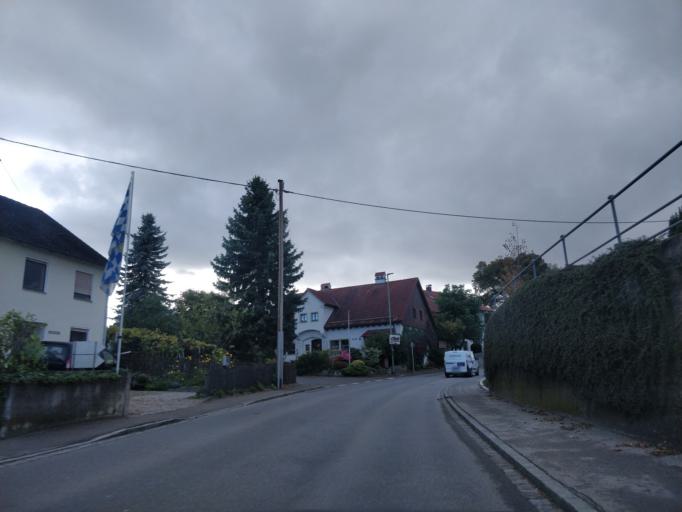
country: DE
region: Bavaria
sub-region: Swabia
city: Ried
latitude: 48.2829
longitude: 11.0218
